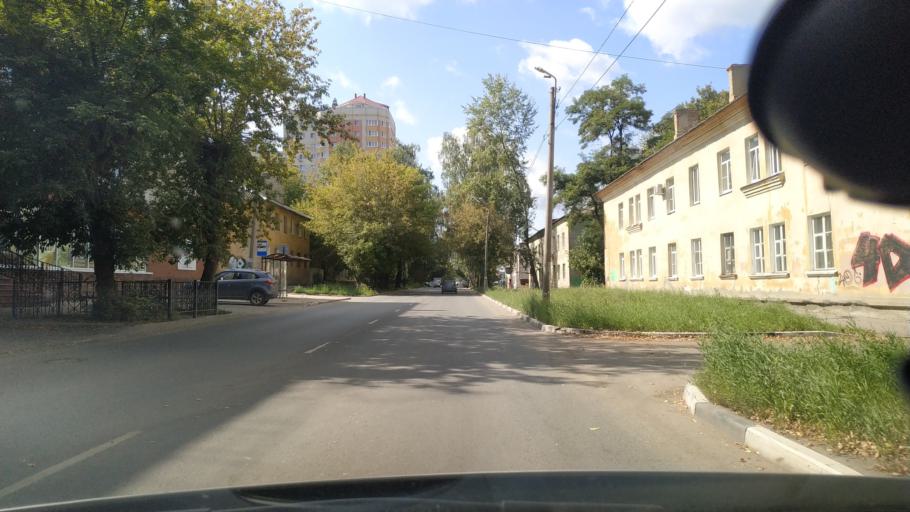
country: RU
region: Rjazan
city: Ryazan'
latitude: 54.6118
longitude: 39.7055
